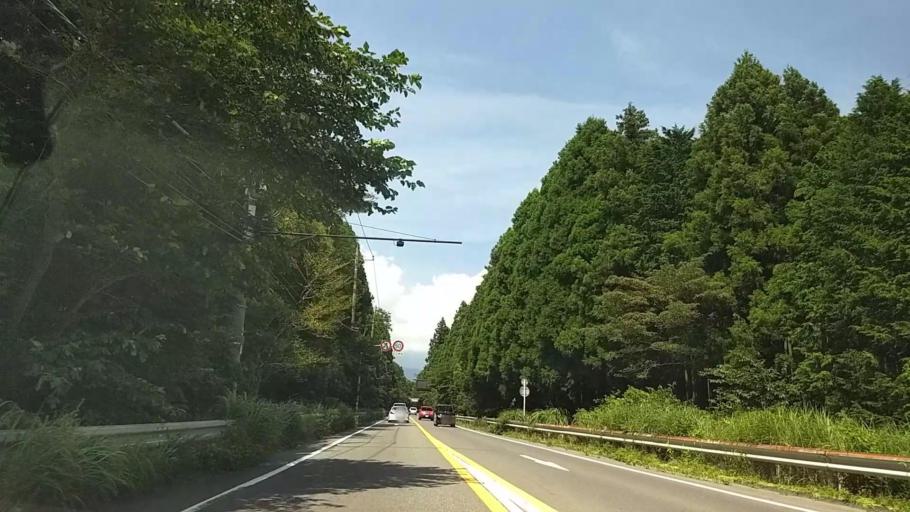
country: JP
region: Shizuoka
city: Fujinomiya
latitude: 35.3298
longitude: 138.5857
